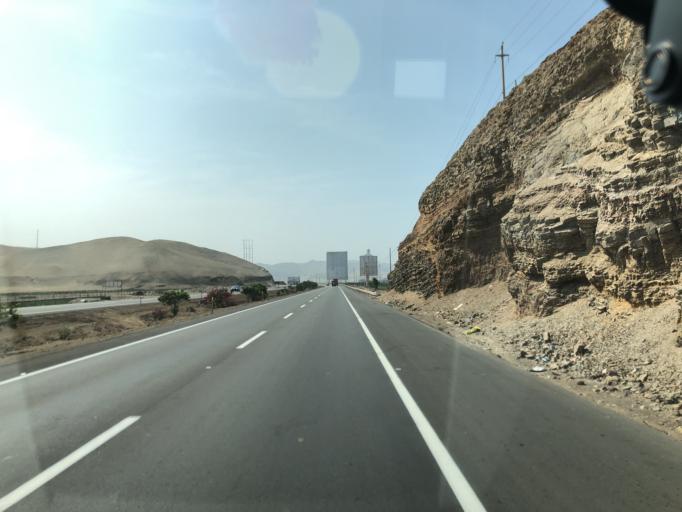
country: PE
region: Lima
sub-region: Provincia de Canete
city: Chilca
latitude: -12.5552
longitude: -76.7113
